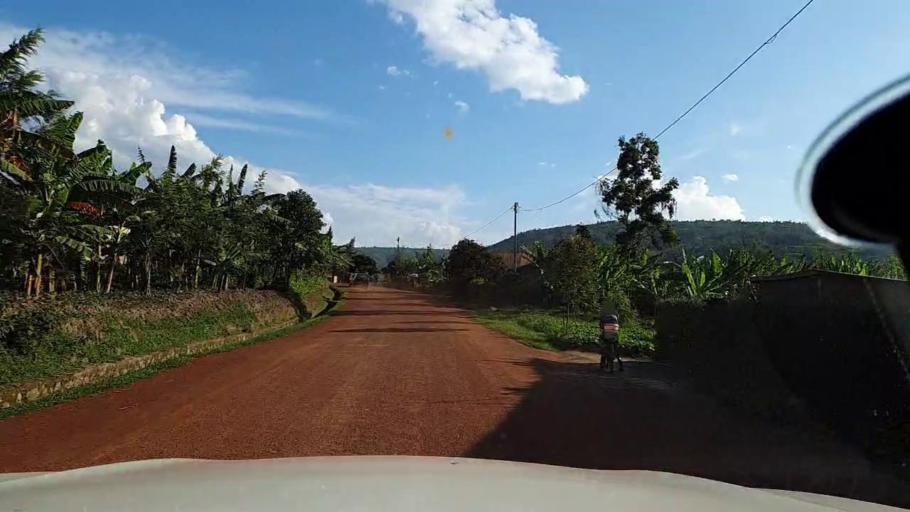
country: RW
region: Kigali
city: Kigali
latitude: -1.8630
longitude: 29.9201
